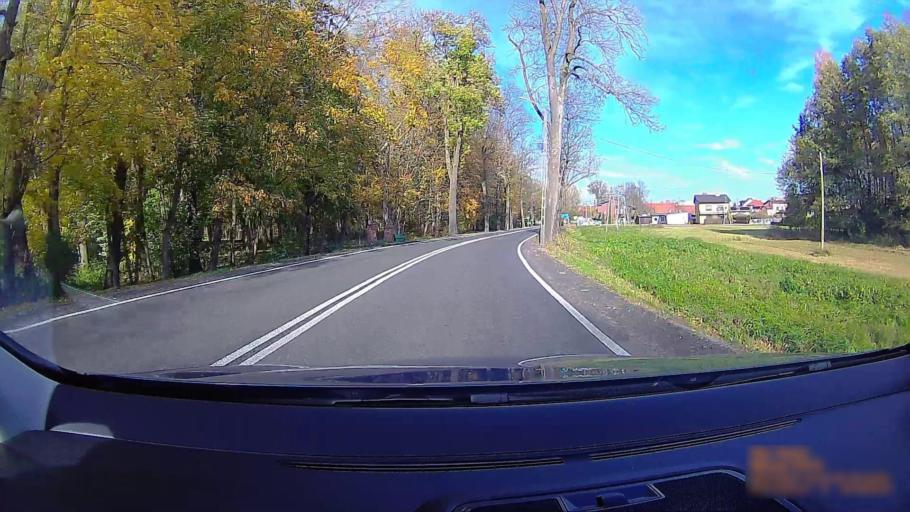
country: PL
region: Greater Poland Voivodeship
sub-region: Powiat ostrzeszowski
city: Doruchow
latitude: 51.4146
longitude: 18.0759
